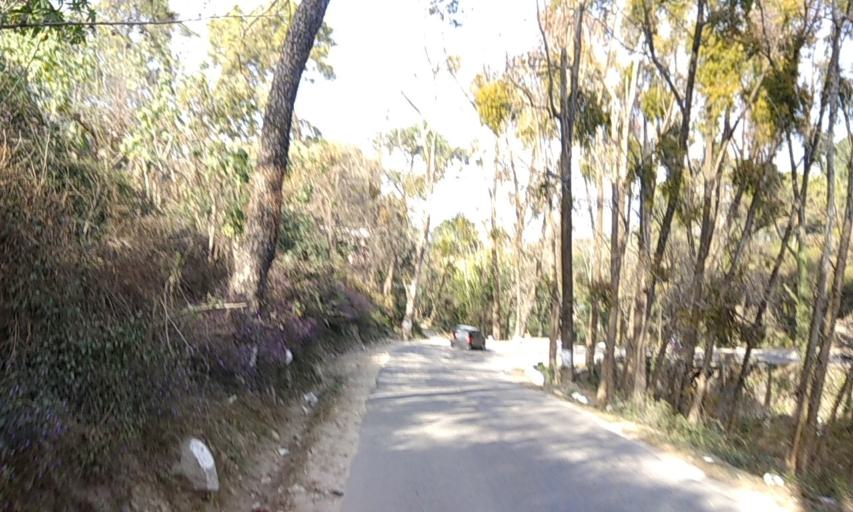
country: IN
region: Himachal Pradesh
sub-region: Kangra
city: Palampur
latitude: 32.0853
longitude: 76.5195
